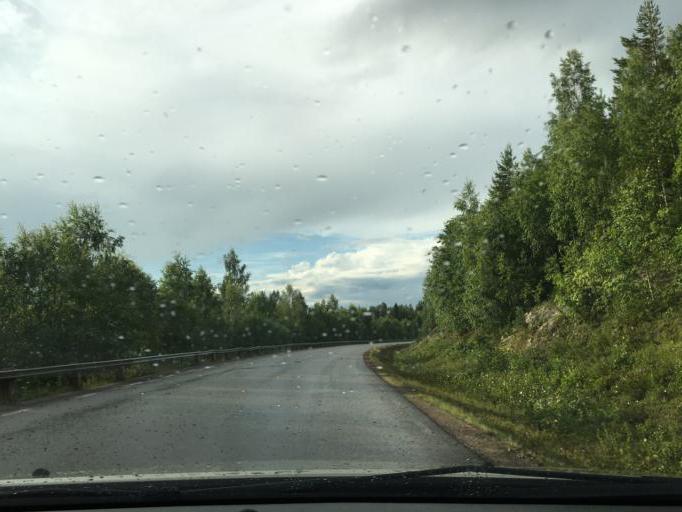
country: SE
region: Norrbotten
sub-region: Kalix Kommun
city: Rolfs
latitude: 65.9331
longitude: 22.8929
